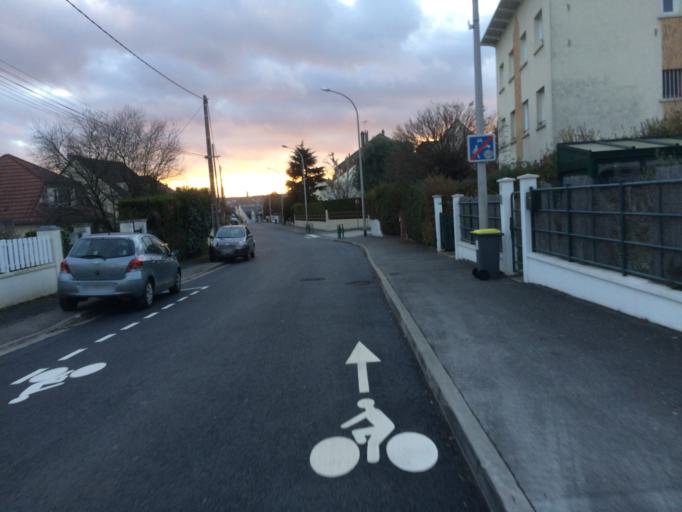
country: FR
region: Ile-de-France
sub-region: Departement de l'Essonne
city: Verrieres-le-Buisson
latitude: 48.7431
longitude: 2.2558
